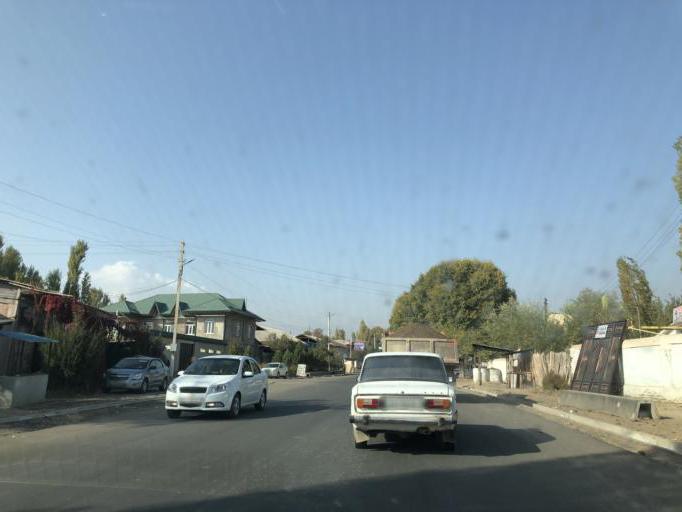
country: UZ
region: Namangan
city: Chust Shahri
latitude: 41.0715
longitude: 71.2046
